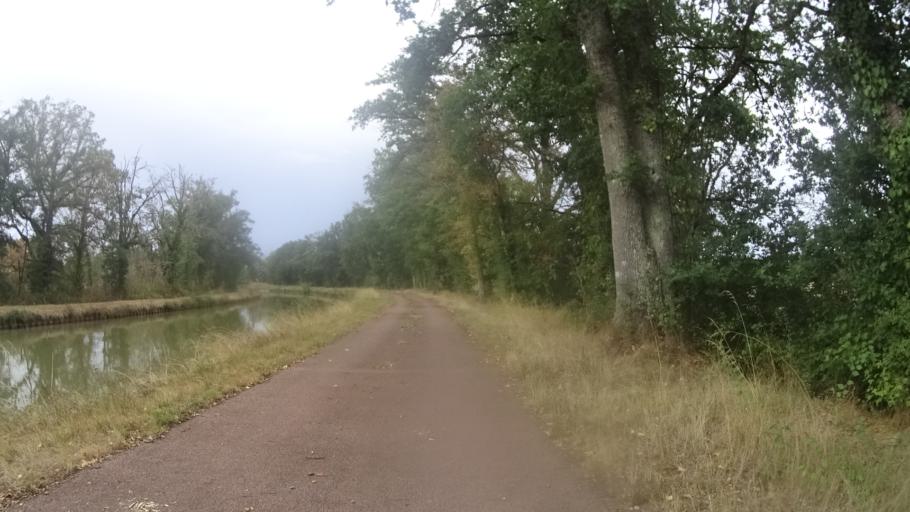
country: FR
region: Bourgogne
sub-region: Departement de la Nievre
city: Imphy
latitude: 46.9075
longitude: 3.2495
